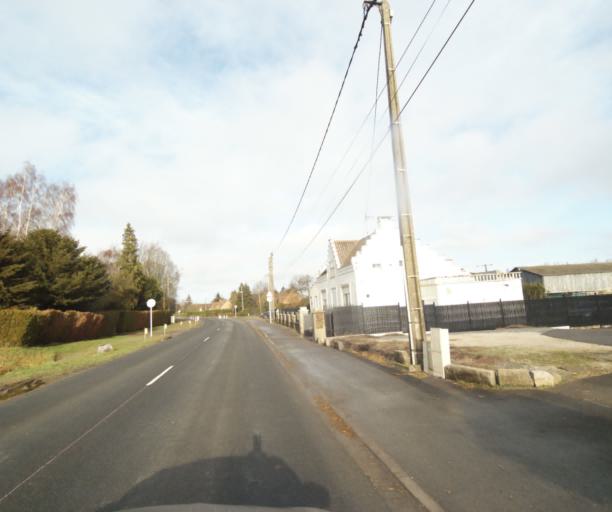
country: FR
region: Nord-Pas-de-Calais
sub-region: Departement du Nord
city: Thiant
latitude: 50.2818
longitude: 3.4519
